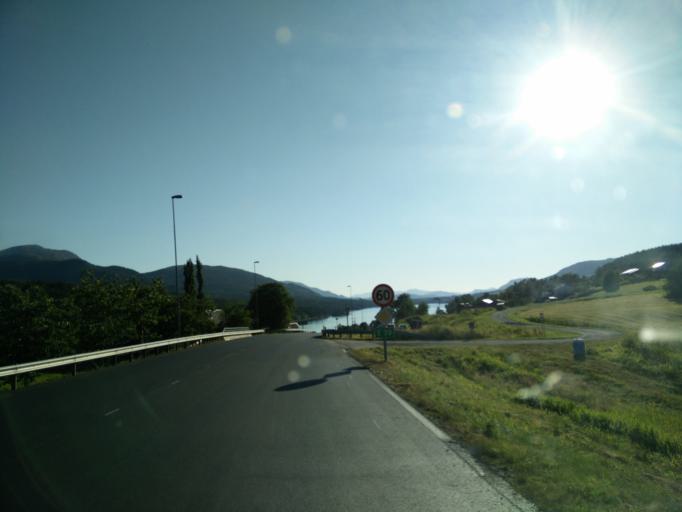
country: NO
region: More og Romsdal
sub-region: Halsa
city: Liaboen
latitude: 63.0882
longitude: 8.3539
